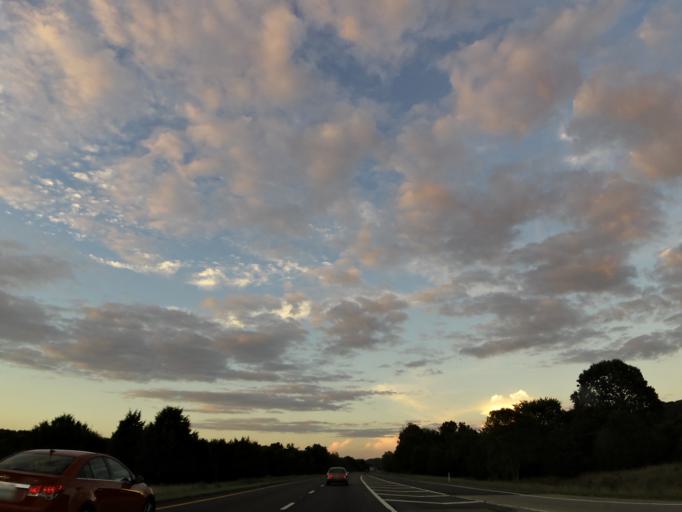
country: US
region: Tennessee
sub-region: Monroe County
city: Sweetwater
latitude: 35.6253
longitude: -84.4885
